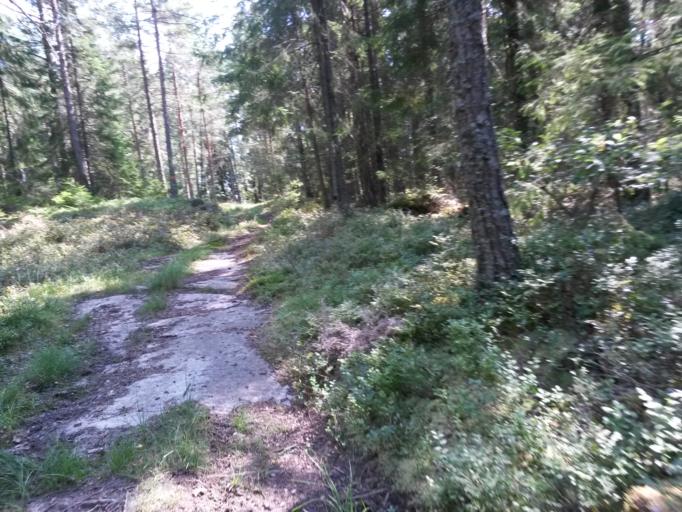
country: SE
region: Vaestra Goetaland
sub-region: Vargarda Kommun
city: Jonstorp
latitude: 57.9563
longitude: 12.6841
